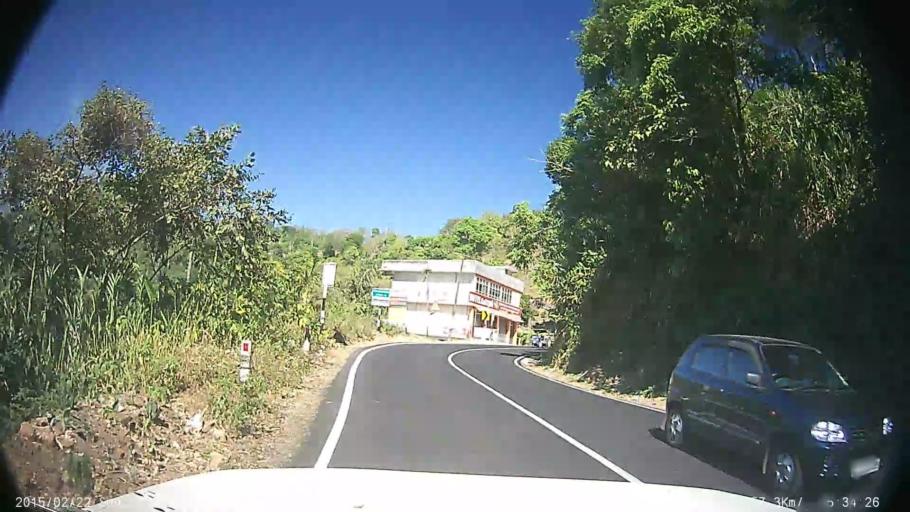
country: IN
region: Kerala
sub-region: Kottayam
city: Erattupetta
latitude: 9.5544
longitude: 76.9712
